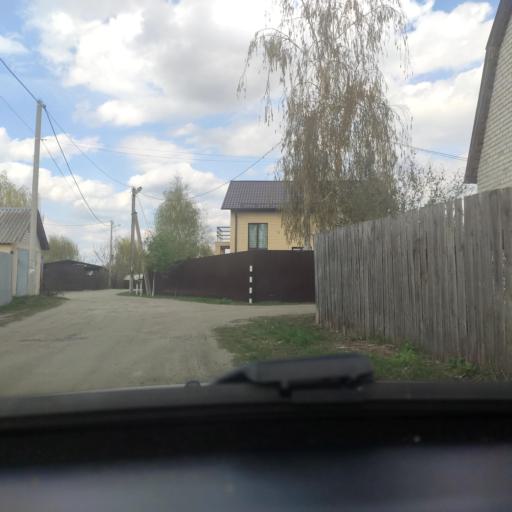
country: RU
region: Voronezj
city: Somovo
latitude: 51.6952
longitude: 39.3688
